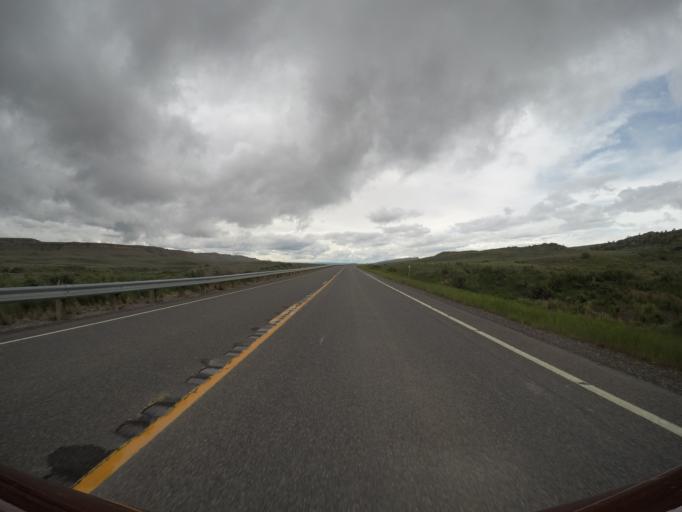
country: US
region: Wyoming
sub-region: Park County
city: Powell
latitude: 45.0971
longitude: -108.7249
